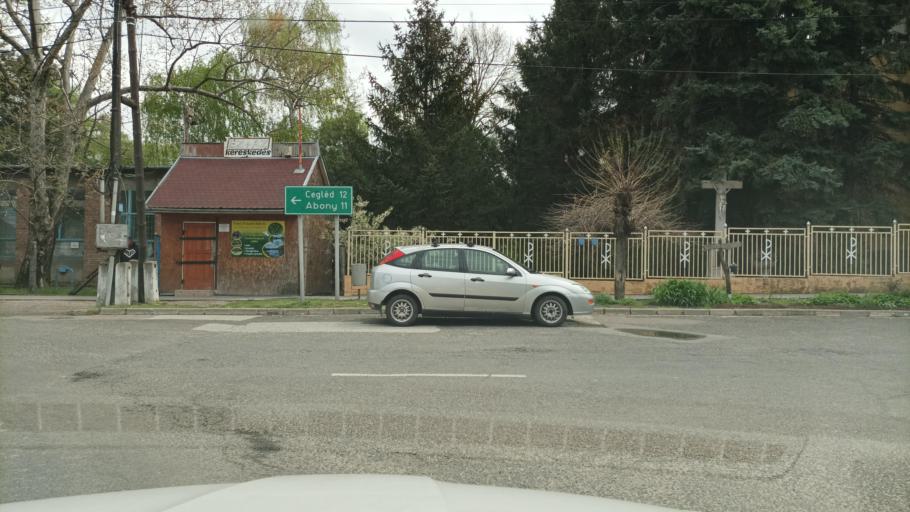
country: HU
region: Pest
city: Tortel
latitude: 47.1181
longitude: 19.9319
